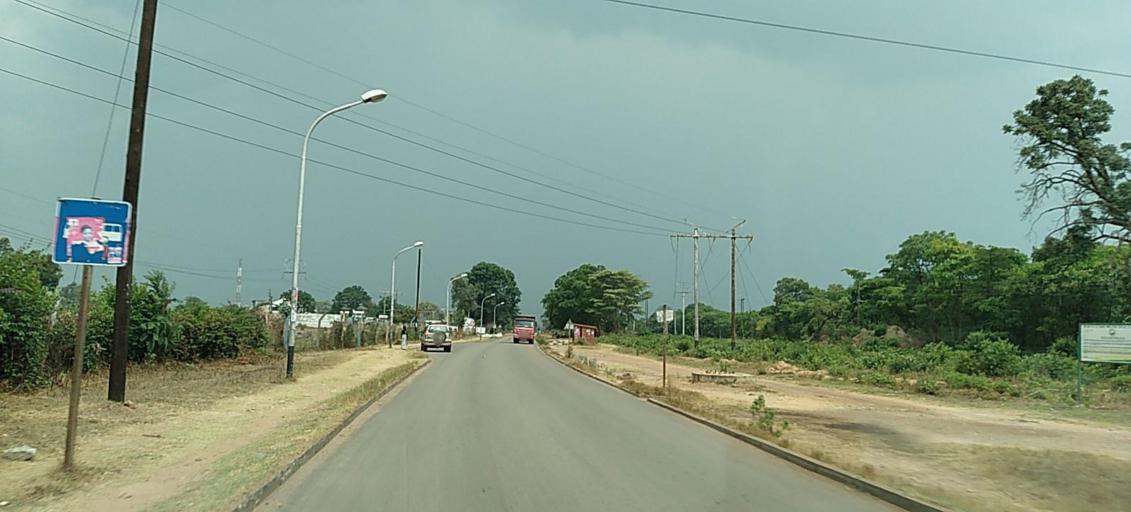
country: ZM
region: Copperbelt
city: Kalulushi
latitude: -12.8326
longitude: 28.1026
